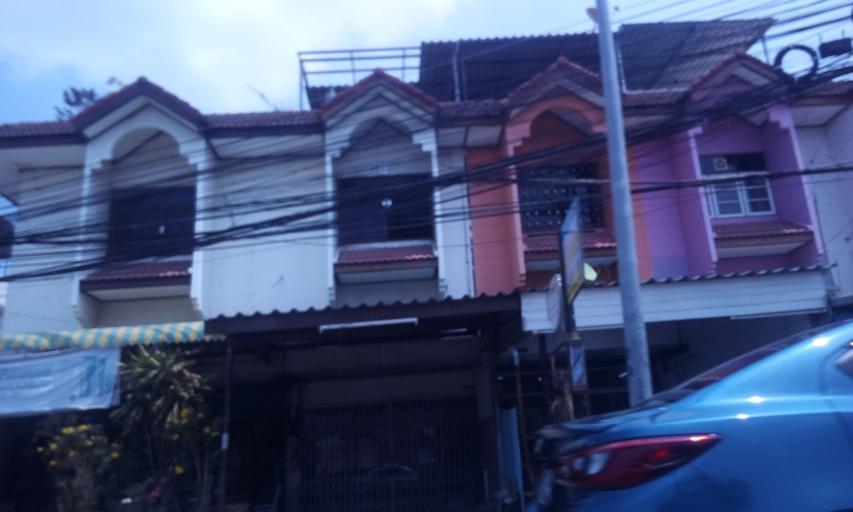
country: TH
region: Chachoengsao
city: Chachoengsao
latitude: 13.6997
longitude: 101.0917
